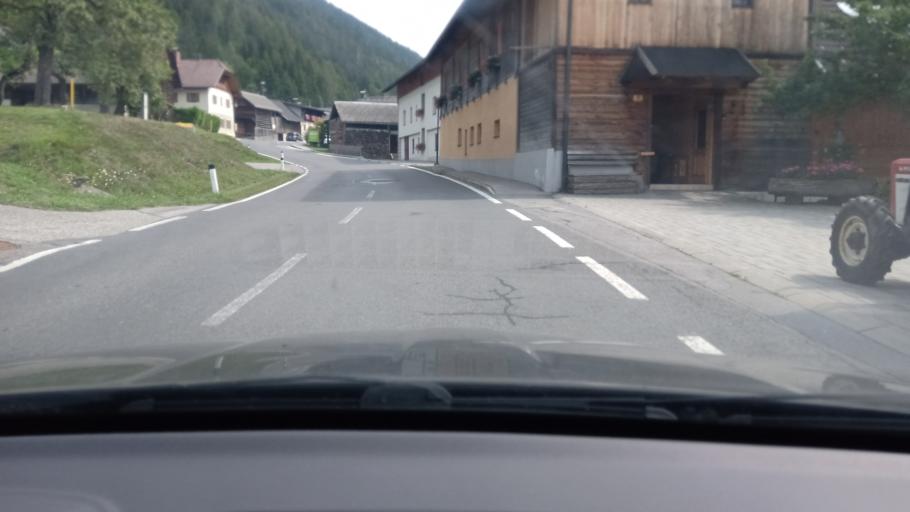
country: AT
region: Carinthia
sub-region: Politischer Bezirk Spittal an der Drau
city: Steinfeld
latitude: 46.7232
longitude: 13.2708
